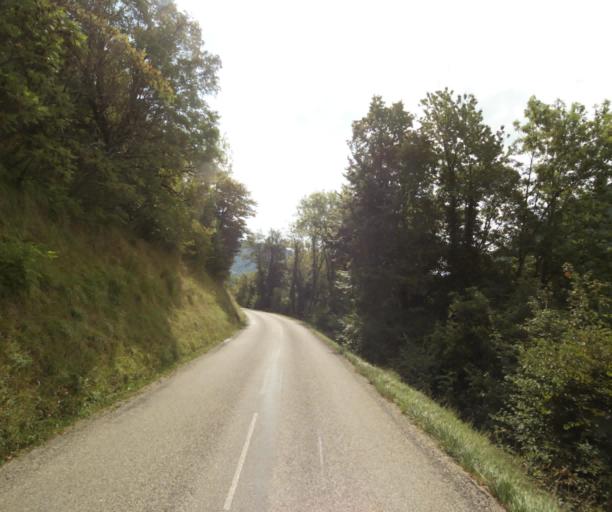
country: FR
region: Rhone-Alpes
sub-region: Departement de l'Isere
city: Saint-Egreve
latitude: 45.2538
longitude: 5.7137
